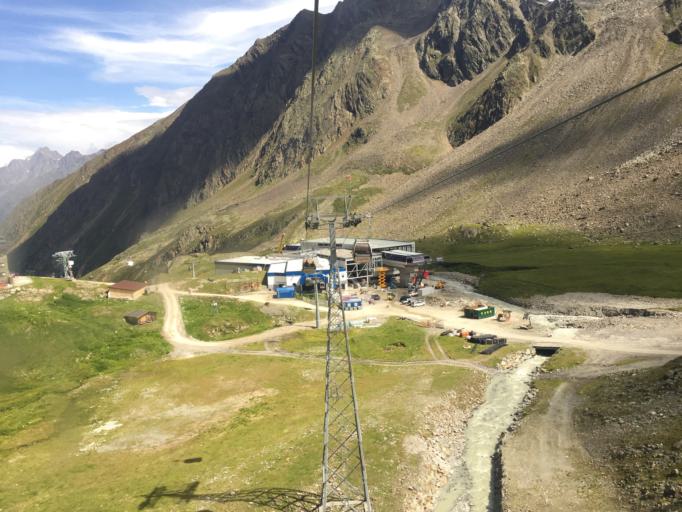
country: AT
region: Tyrol
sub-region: Politischer Bezirk Imst
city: Soelden
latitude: 46.9971
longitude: 11.1373
